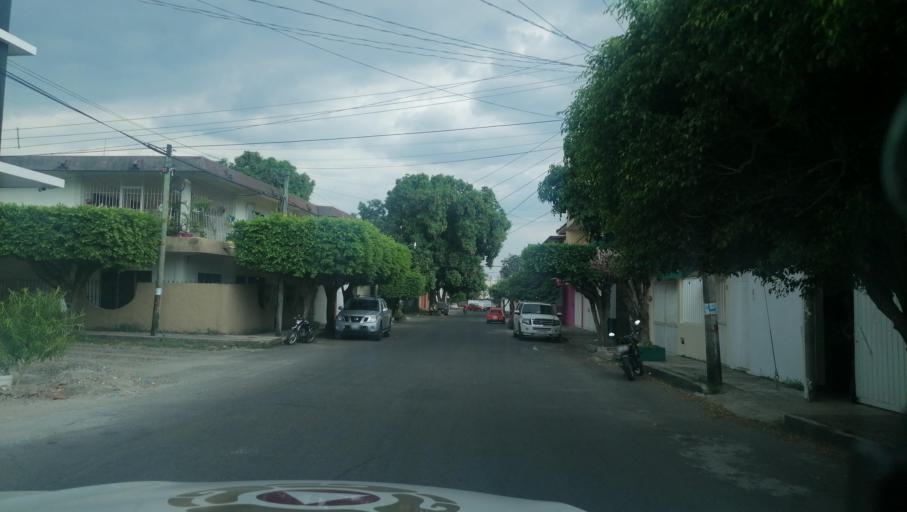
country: MX
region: Chiapas
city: Tapachula
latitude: 14.9186
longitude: -92.2541
